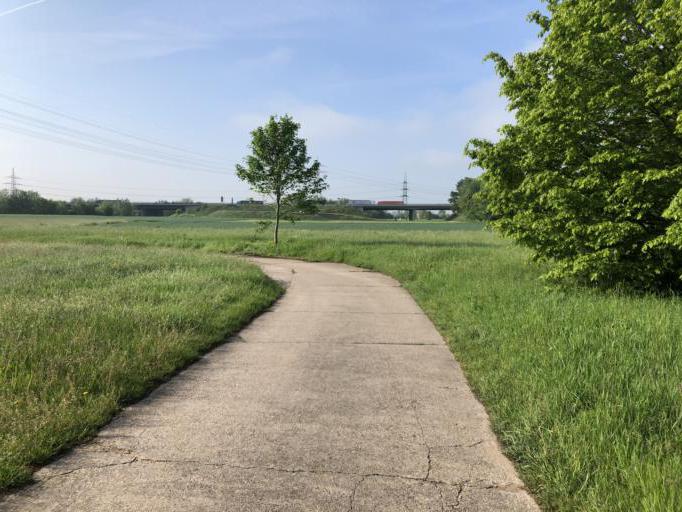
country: DE
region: Bavaria
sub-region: Regierungsbezirk Mittelfranken
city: Erlangen
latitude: 49.5632
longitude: 10.9794
